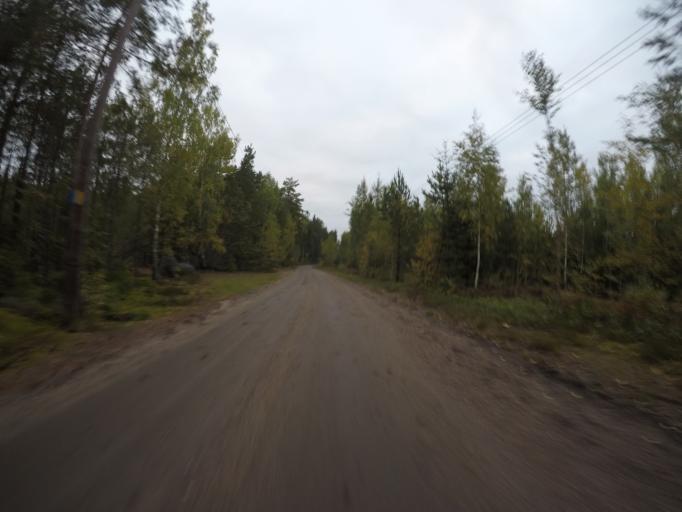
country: SE
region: Vaestmanland
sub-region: Kungsors Kommun
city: Kungsoer
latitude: 59.3804
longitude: 16.1155
